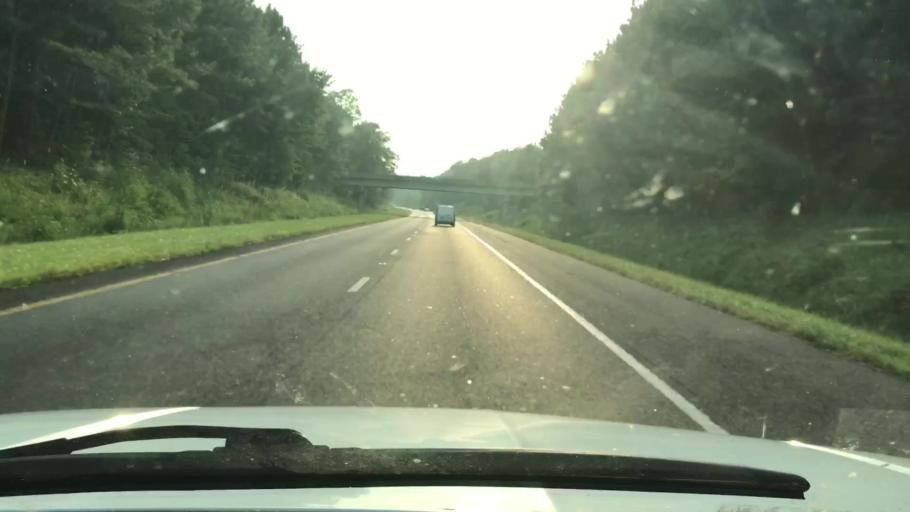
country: US
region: Virginia
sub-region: Chesterfield County
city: Brandermill
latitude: 37.4115
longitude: -77.5894
